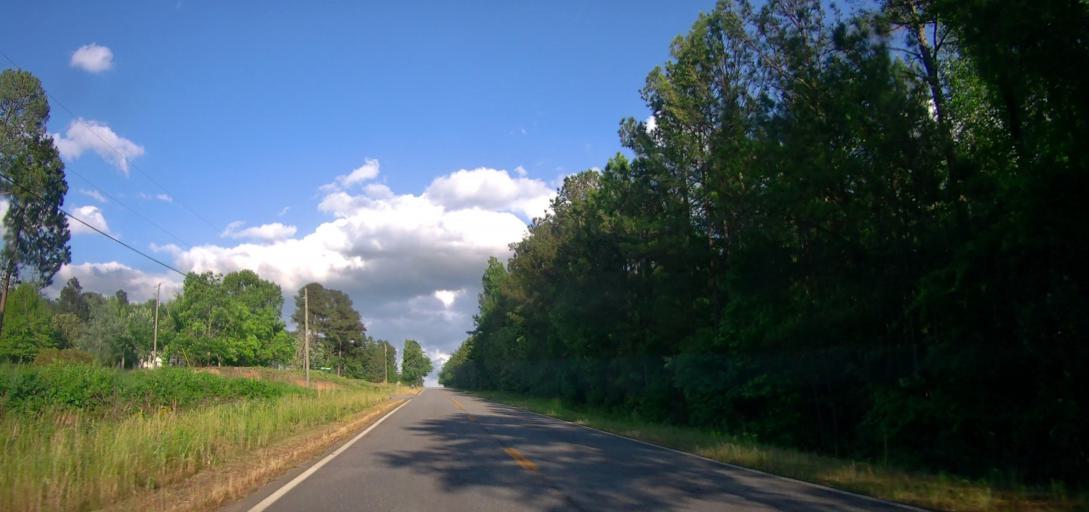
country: US
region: Georgia
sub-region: Peach County
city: Byron
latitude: 32.6769
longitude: -83.7710
